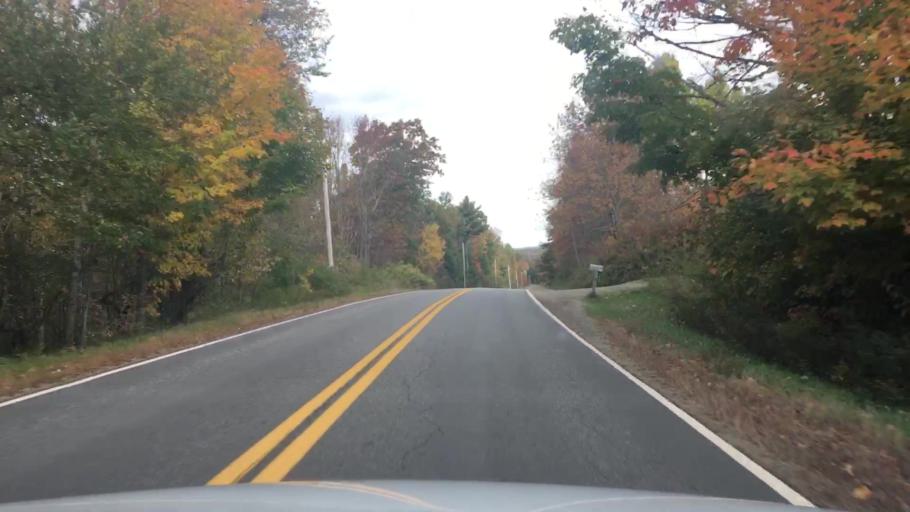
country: US
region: Maine
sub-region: Waldo County
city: Searsmont
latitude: 44.3419
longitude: -69.1392
